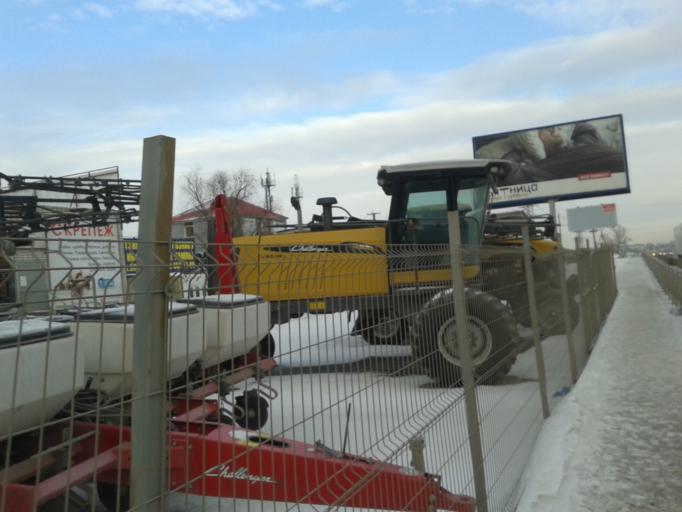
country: RU
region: Volgograd
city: Volgograd
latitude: 48.7610
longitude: 44.5047
